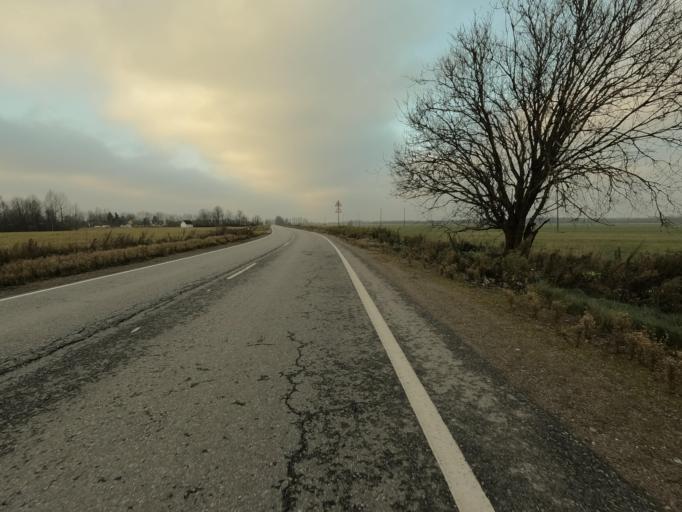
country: RU
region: Leningrad
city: Mga
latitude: 59.7552
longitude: 31.0387
